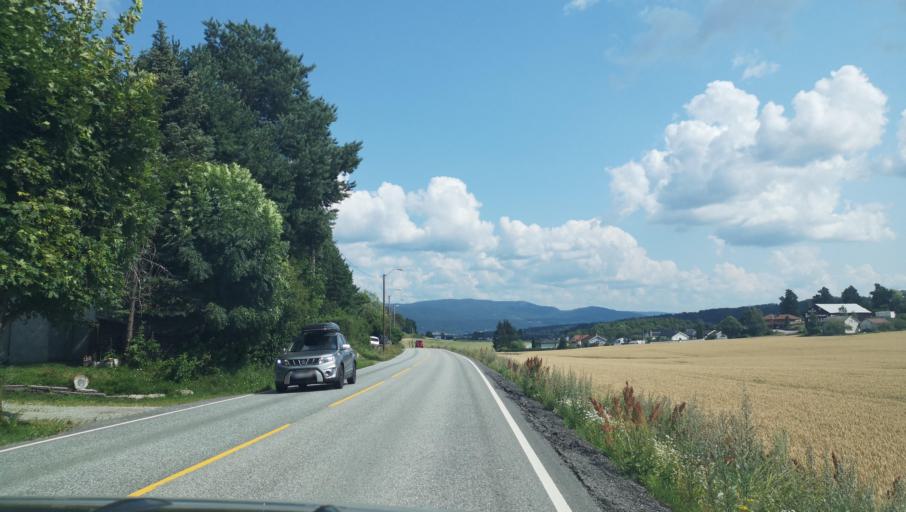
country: NO
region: Buskerud
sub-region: Ovre Eiker
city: Hokksund
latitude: 59.7365
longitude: 9.8530
